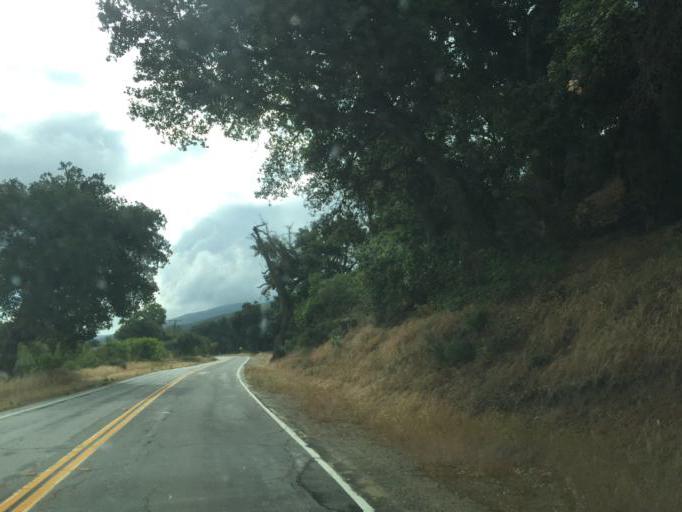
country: US
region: California
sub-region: Los Angeles County
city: Leona Valley
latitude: 34.5834
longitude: -118.3484
